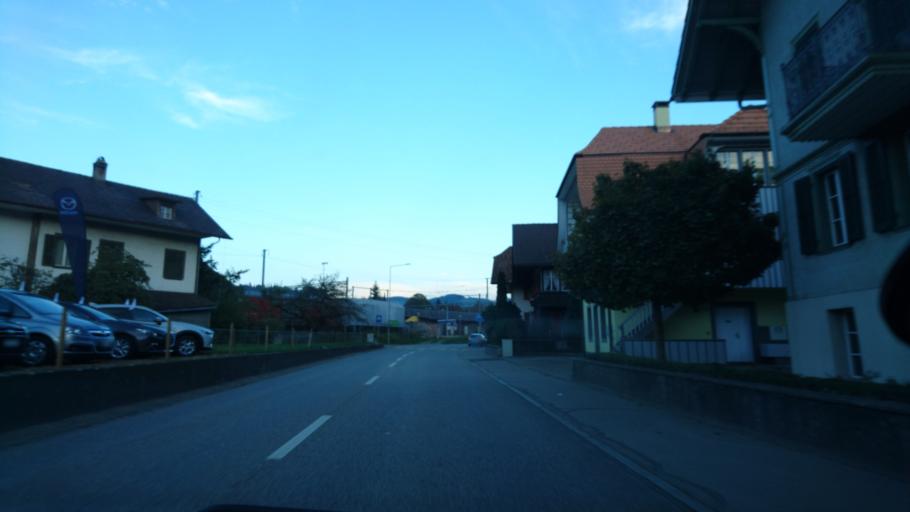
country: CH
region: Bern
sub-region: Emmental District
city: Langnau
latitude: 46.9385
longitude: 7.7833
